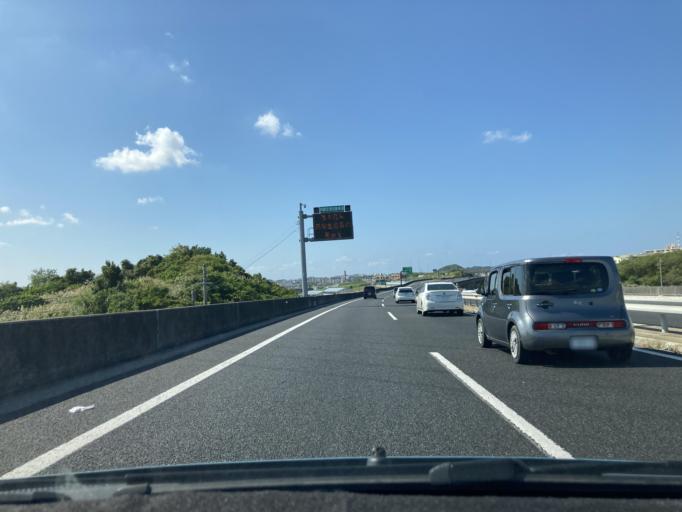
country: JP
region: Okinawa
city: Tomigusuku
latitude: 26.1820
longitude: 127.7320
